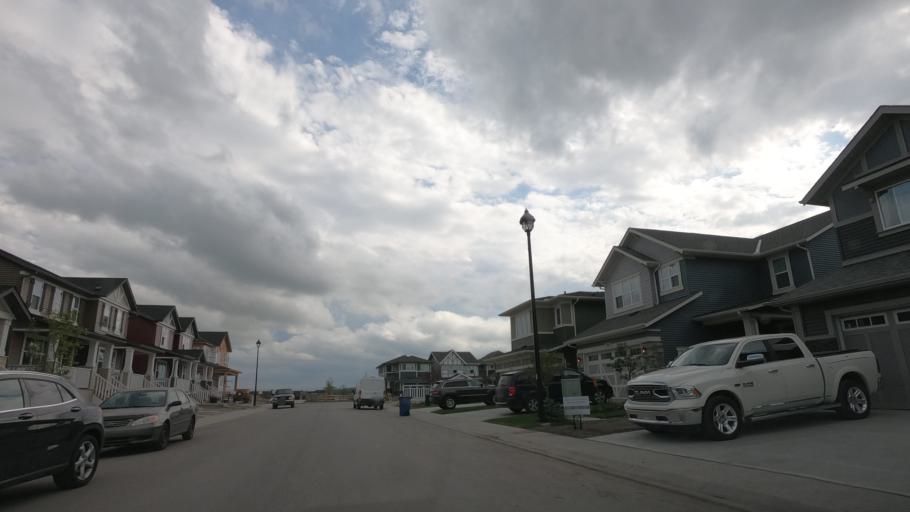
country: CA
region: Alberta
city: Airdrie
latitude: 51.2574
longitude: -113.9829
